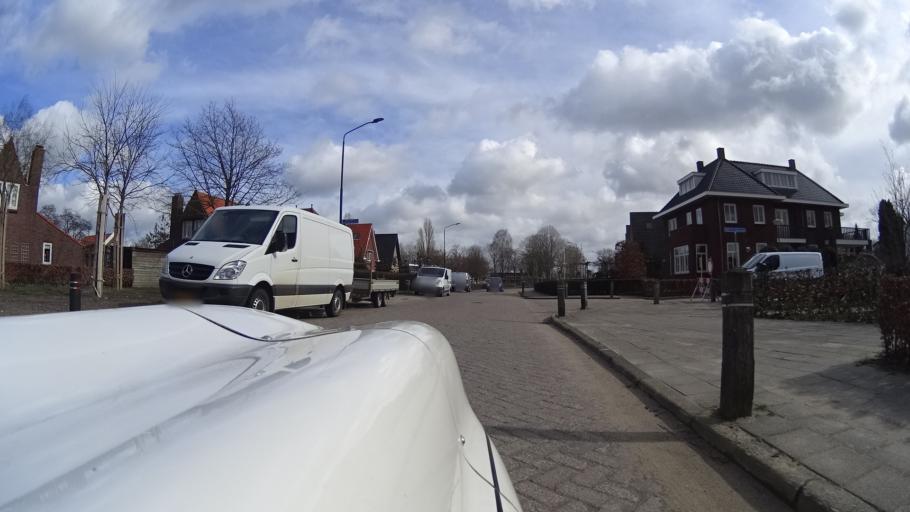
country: NL
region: North Brabant
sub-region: Gemeente Woudrichem
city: Woudrichem
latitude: 51.8135
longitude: 5.0008
